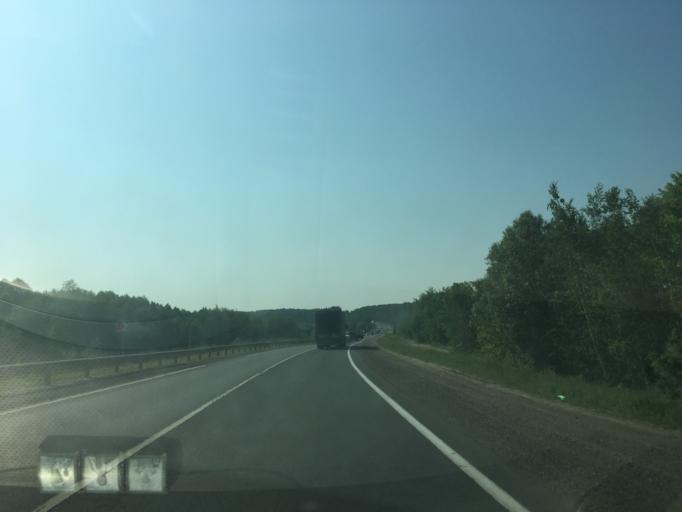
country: RU
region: Nizjnij Novgorod
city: Pamyat' Parizhskoy Kommuny
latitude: 56.0763
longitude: 44.3705
